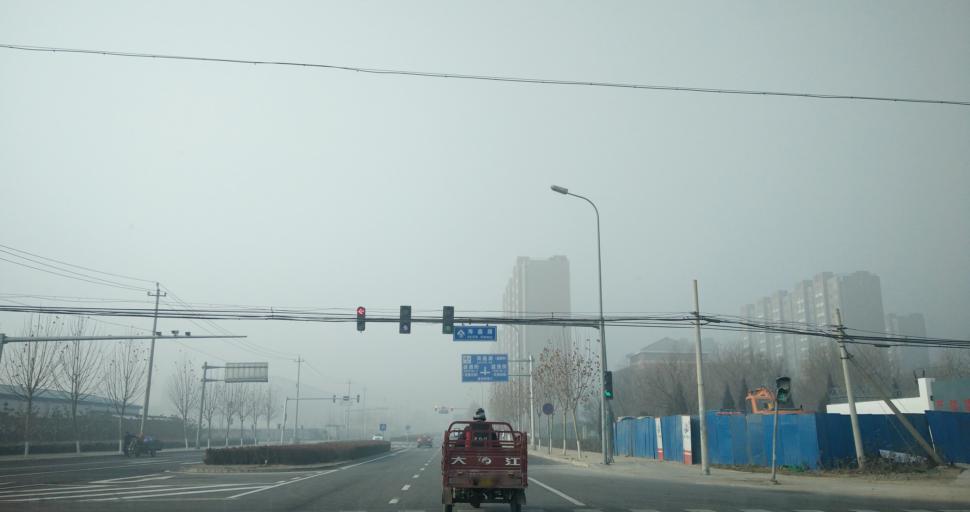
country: CN
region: Beijing
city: Yinghai
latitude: 39.7085
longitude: 116.4025
